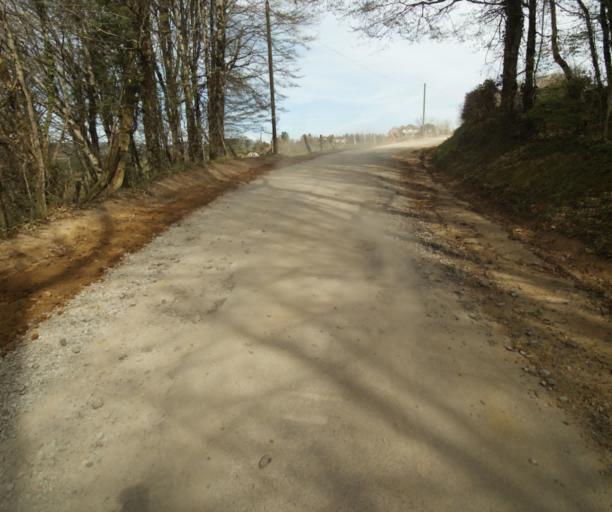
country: FR
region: Limousin
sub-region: Departement de la Correze
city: Naves
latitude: 45.2944
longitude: 1.7785
